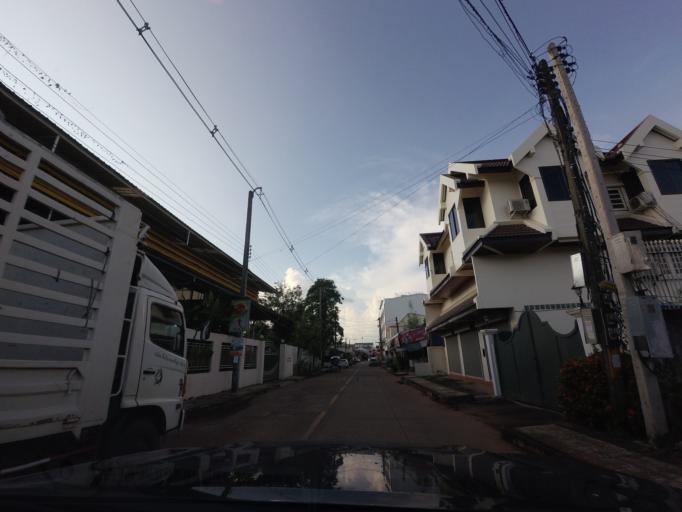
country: TH
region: Nong Khai
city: Nong Khai
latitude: 17.8798
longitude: 102.7479
